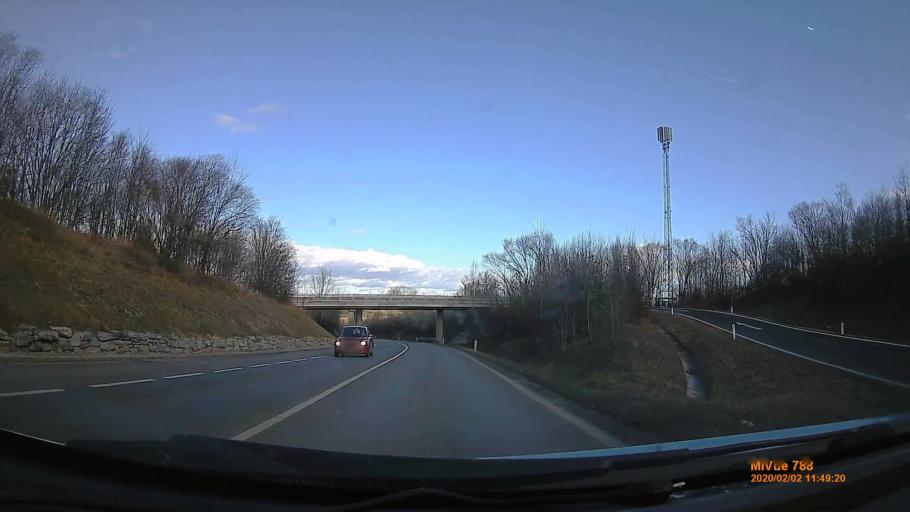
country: AT
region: Burgenland
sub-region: Eisenstadt-Umgebung
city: Klingenbach
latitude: 47.7512
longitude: 16.5466
